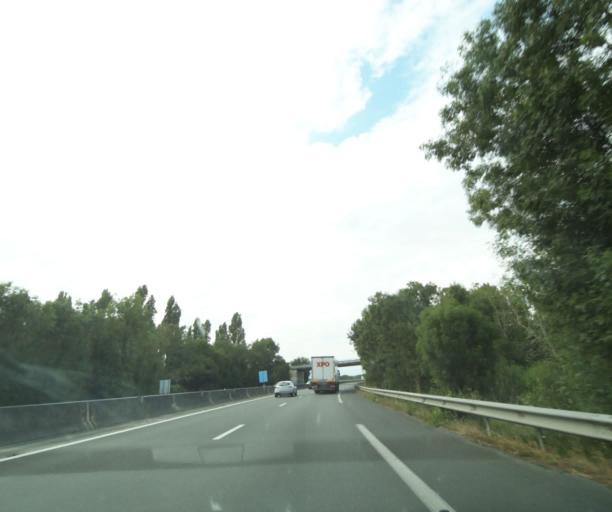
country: FR
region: Poitou-Charentes
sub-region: Departement de la Charente-Maritime
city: Aytre
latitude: 46.1223
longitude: -1.1098
